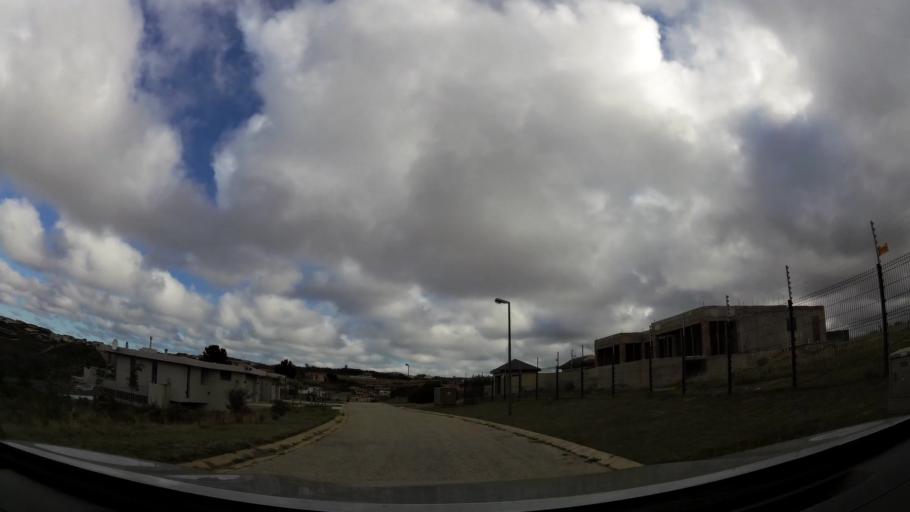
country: ZA
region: Western Cape
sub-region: Eden District Municipality
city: Plettenberg Bay
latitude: -34.0829
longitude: 23.3572
